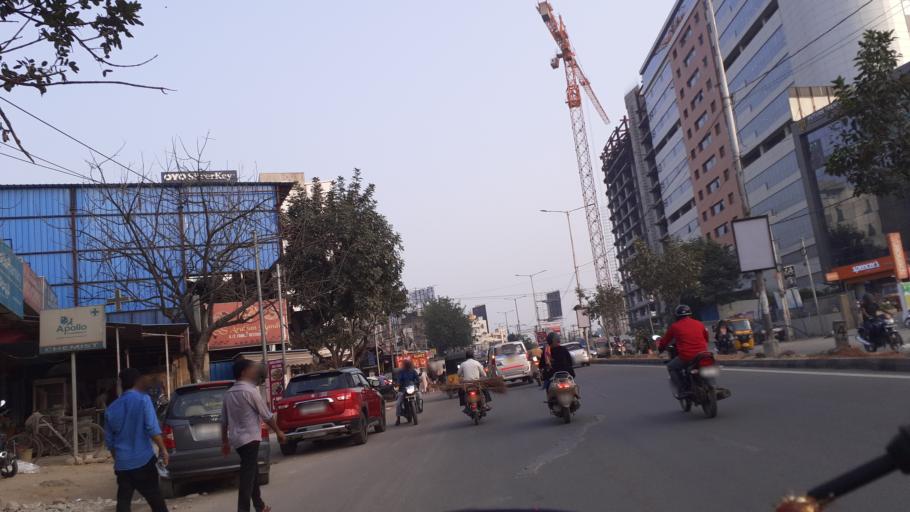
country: IN
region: Telangana
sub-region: Rangareddi
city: Kukatpalli
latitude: 17.4864
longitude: 78.3580
